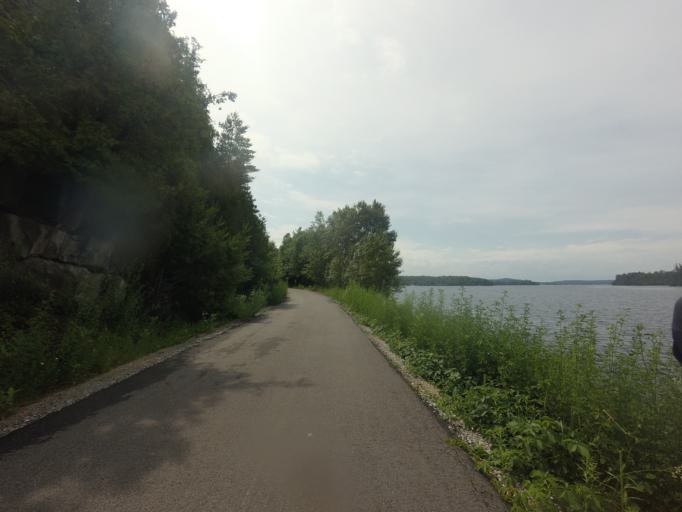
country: CA
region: Quebec
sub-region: Outaouais
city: Maniwaki
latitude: 46.2148
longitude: -76.0440
